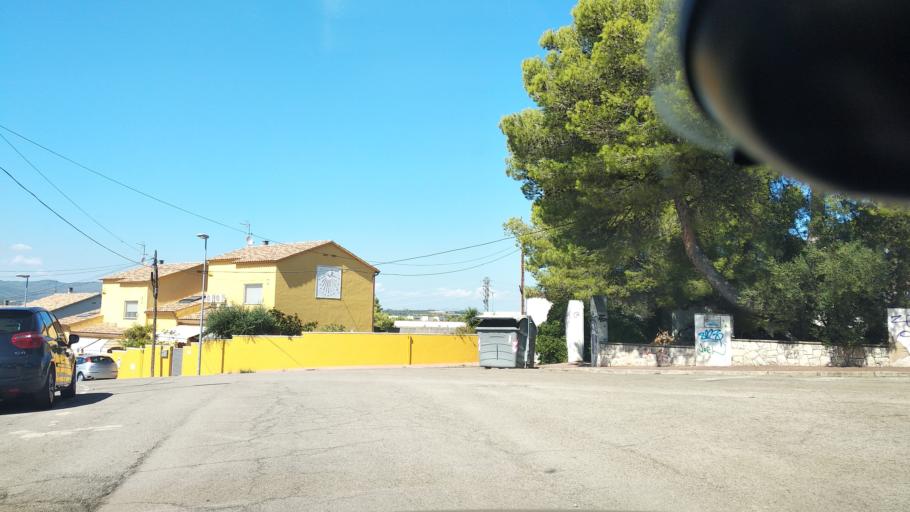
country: ES
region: Catalonia
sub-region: Provincia de Tarragona
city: El Vendrell
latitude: 41.2227
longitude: 1.5443
